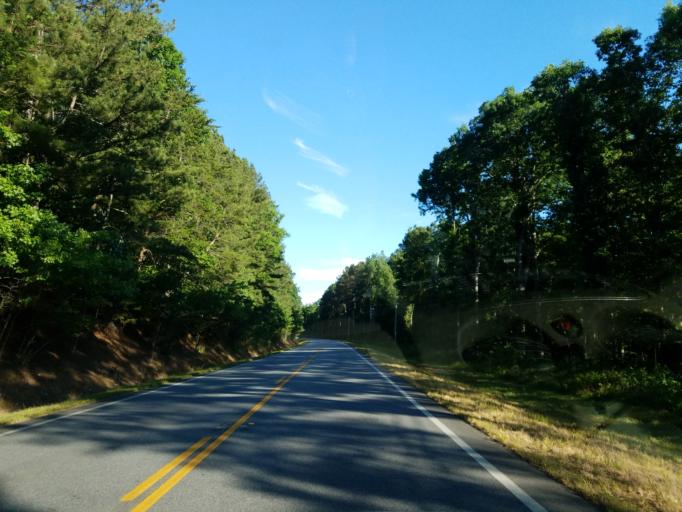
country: US
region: Georgia
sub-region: Gordon County
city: Calhoun
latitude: 34.6146
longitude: -85.0509
